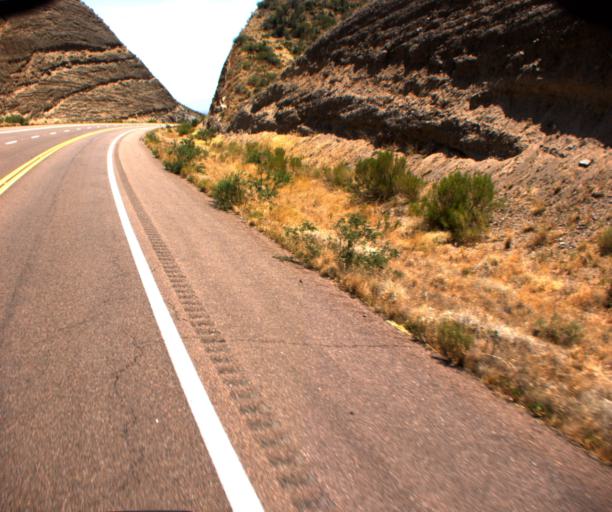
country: US
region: Arizona
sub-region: Gila County
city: Tonto Basin
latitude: 33.9867
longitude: -111.3122
